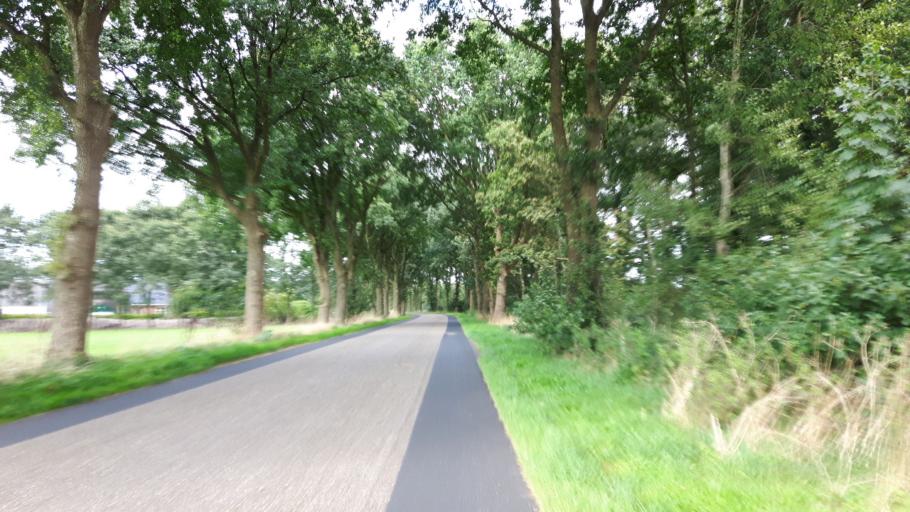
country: NL
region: Groningen
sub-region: Gemeente Leek
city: Leek
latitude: 53.0866
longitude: 6.3174
